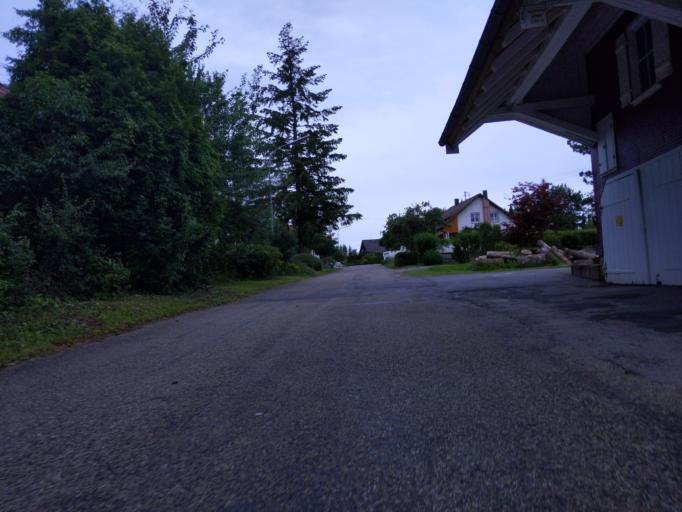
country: DE
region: Baden-Wuerttemberg
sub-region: Karlsruhe Region
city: Alpirsbach
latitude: 48.3372
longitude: 8.4330
